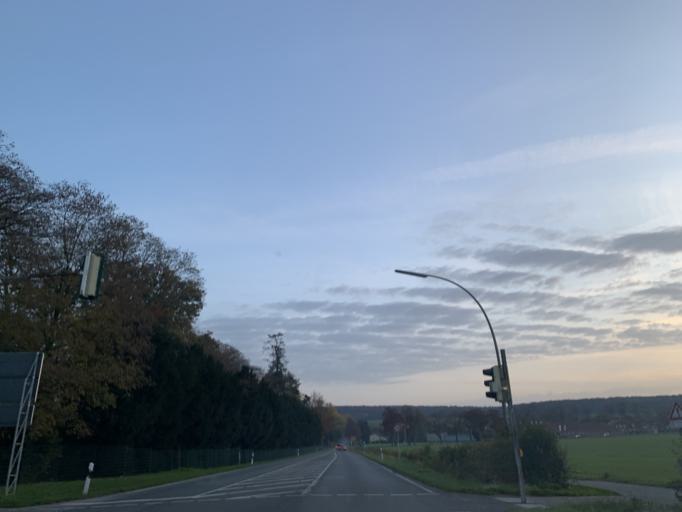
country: DE
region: North Rhine-Westphalia
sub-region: Regierungsbezirk Munster
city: Havixbeck
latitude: 51.9726
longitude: 7.4080
